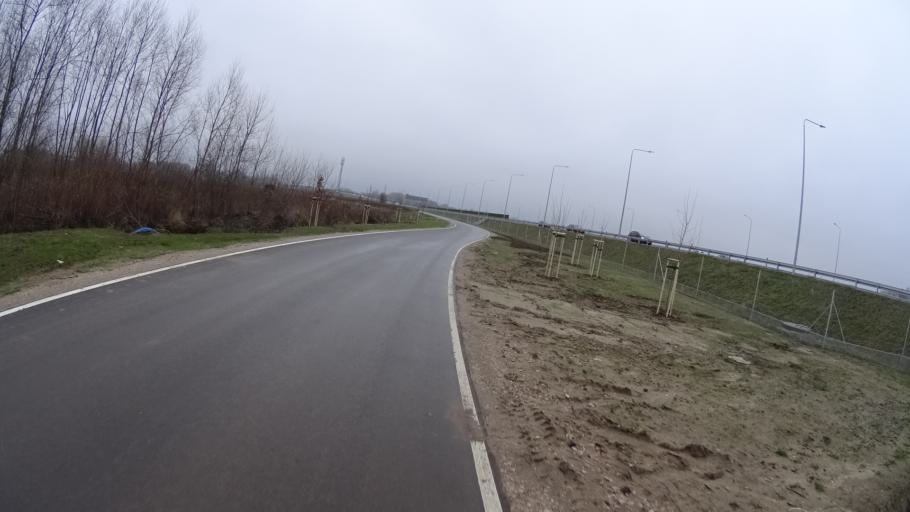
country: PL
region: Masovian Voivodeship
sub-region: Warszawa
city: Wilanow
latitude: 52.1515
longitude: 21.1004
